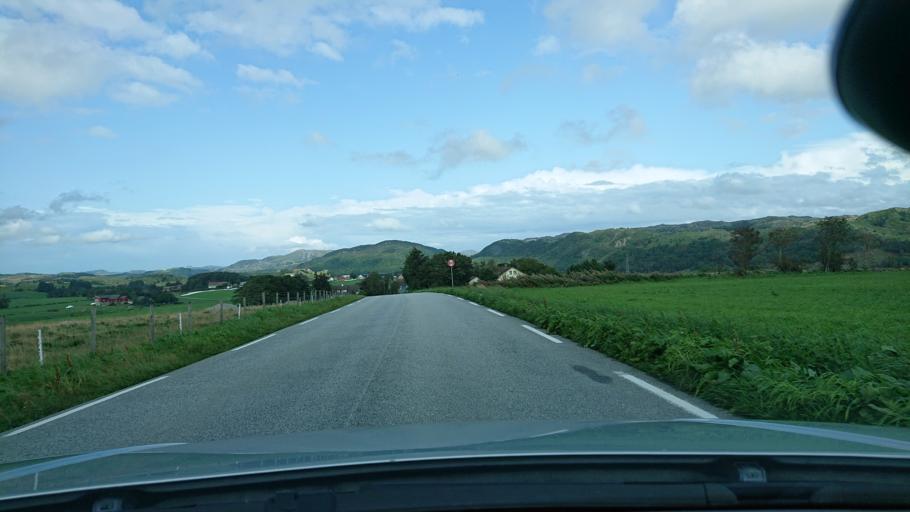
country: NO
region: Rogaland
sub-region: Gjesdal
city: Algard
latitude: 58.6937
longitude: 5.7749
